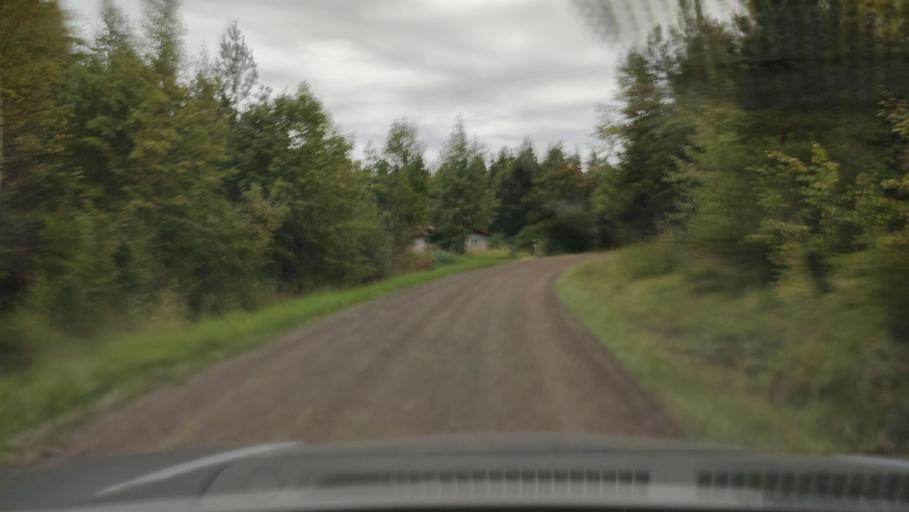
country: FI
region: Southern Ostrobothnia
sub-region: Suupohja
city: Karijoki
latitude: 62.2199
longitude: 21.5721
